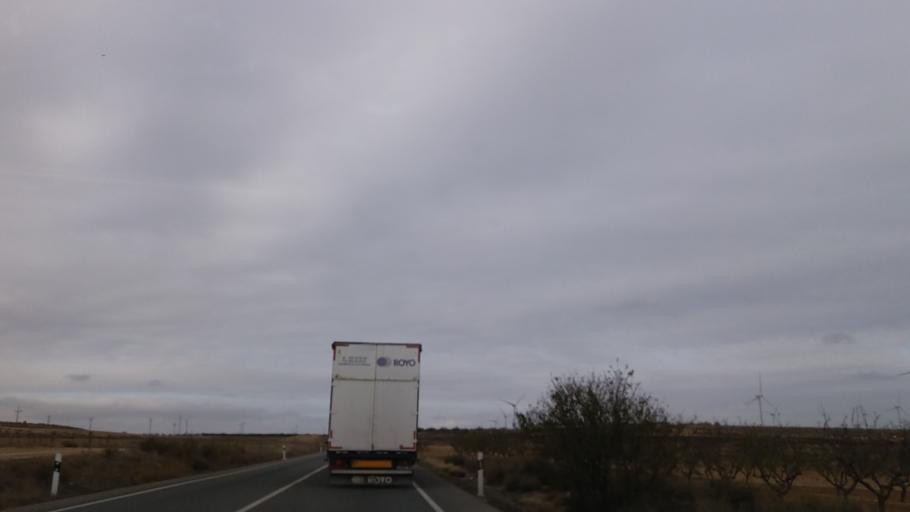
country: ES
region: Aragon
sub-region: Provincia de Zaragoza
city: Mallen
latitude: 41.8659
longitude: -1.3859
